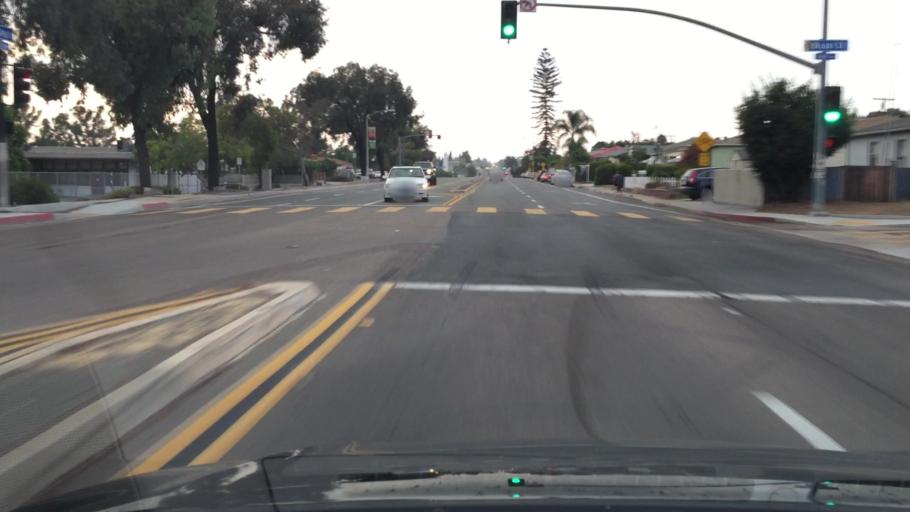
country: US
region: California
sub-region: San Diego County
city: Lemon Grove
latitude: 32.7321
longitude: -117.0797
